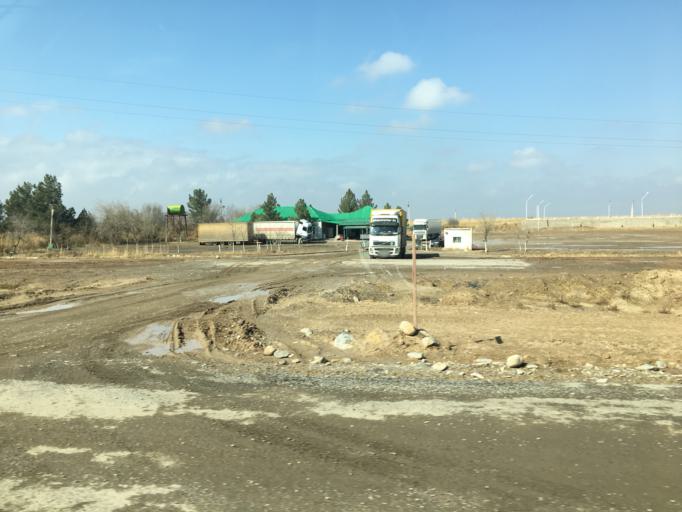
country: IR
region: Razavi Khorasan
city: Sarakhs
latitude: 37.2365
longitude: 61.2328
